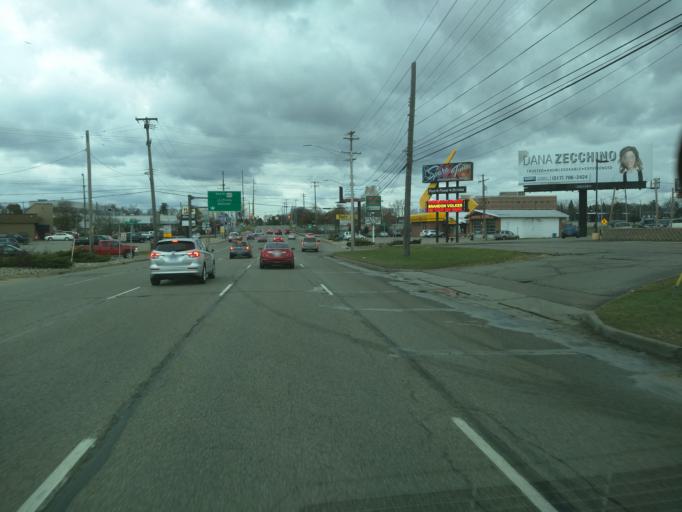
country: US
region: Michigan
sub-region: Ingham County
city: East Lansing
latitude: 42.7417
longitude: -84.5076
